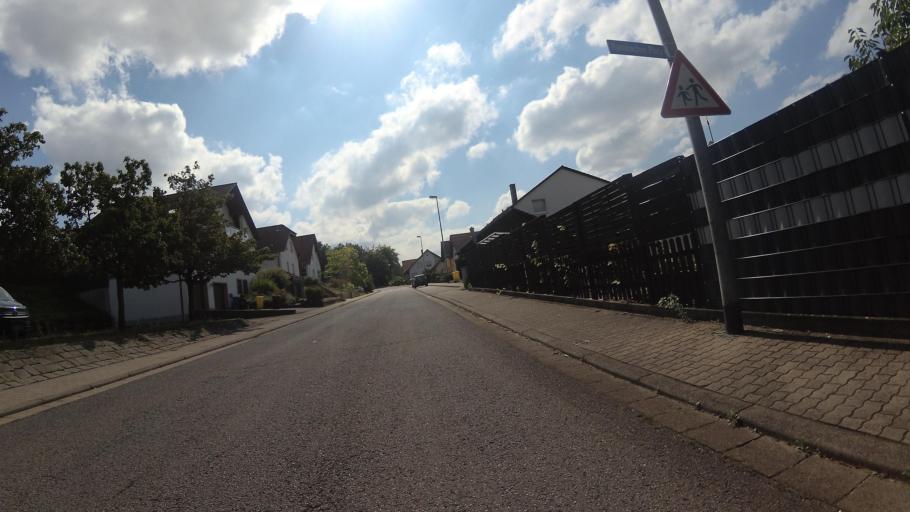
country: DE
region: Rheinland-Pfalz
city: Zweibrucken
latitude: 49.2369
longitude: 7.3710
